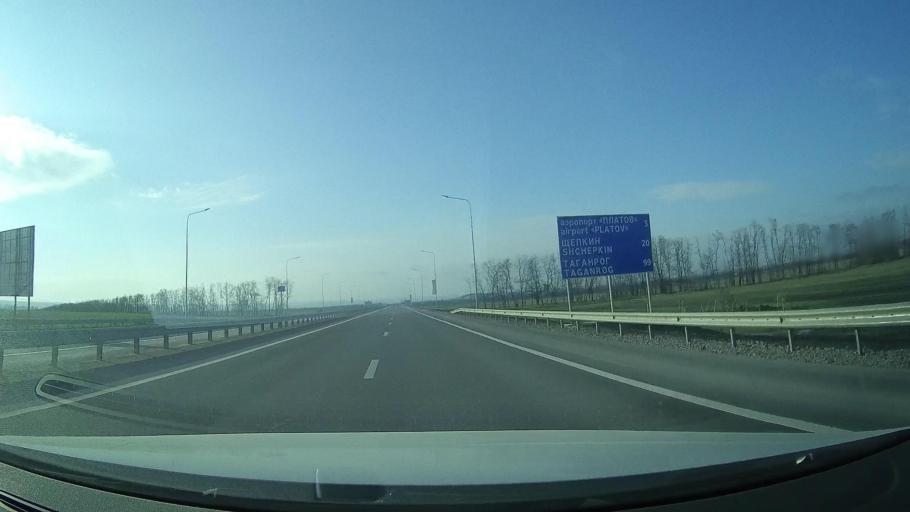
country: RU
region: Rostov
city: Grushevskaya
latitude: 47.5003
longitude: 39.9645
